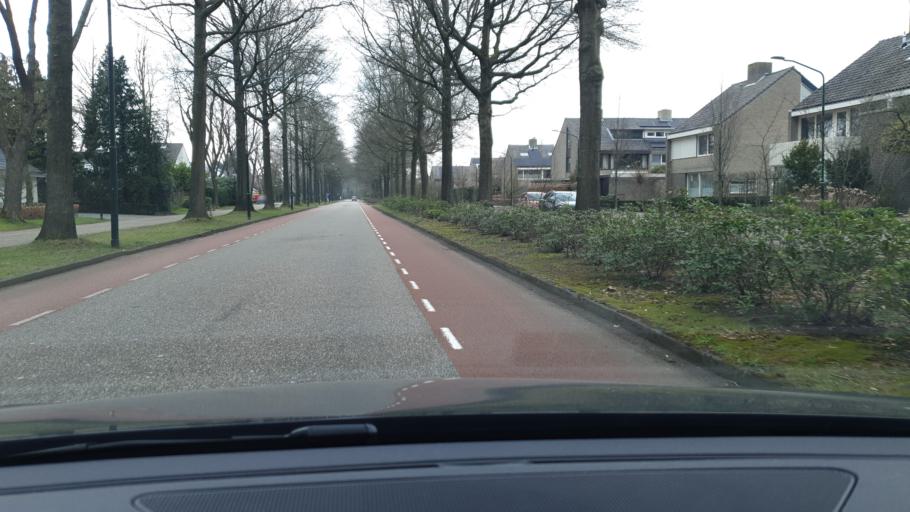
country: NL
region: North Brabant
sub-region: Gemeente Son en Breugel
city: Son
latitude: 51.5206
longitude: 5.4752
